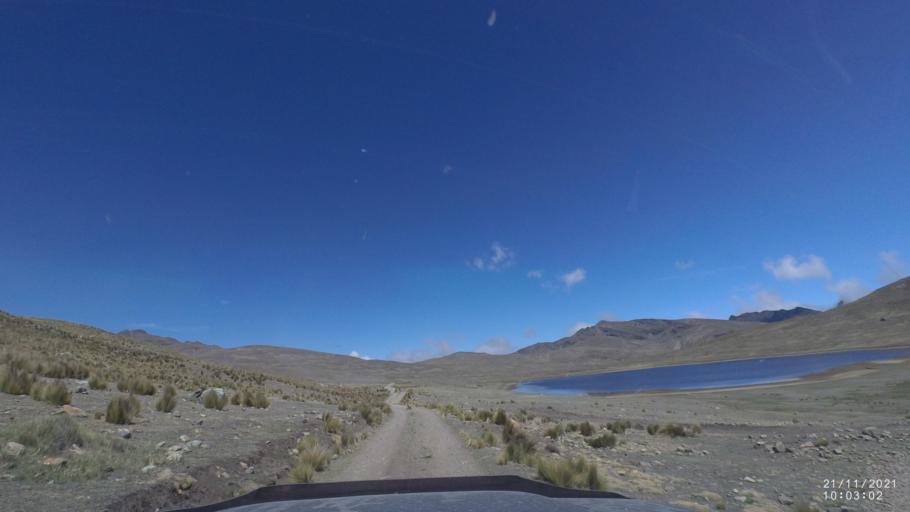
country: BO
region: Cochabamba
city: Cochabamba
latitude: -17.0280
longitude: -66.2770
